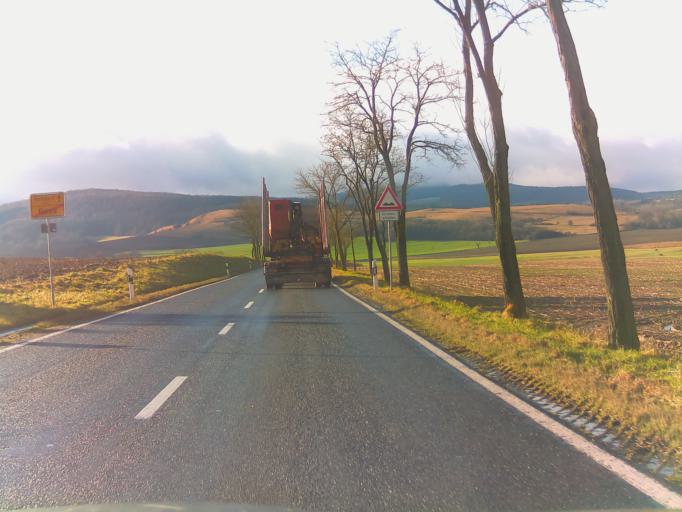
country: DE
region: Thuringia
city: Rosa
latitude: 50.7086
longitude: 10.2453
